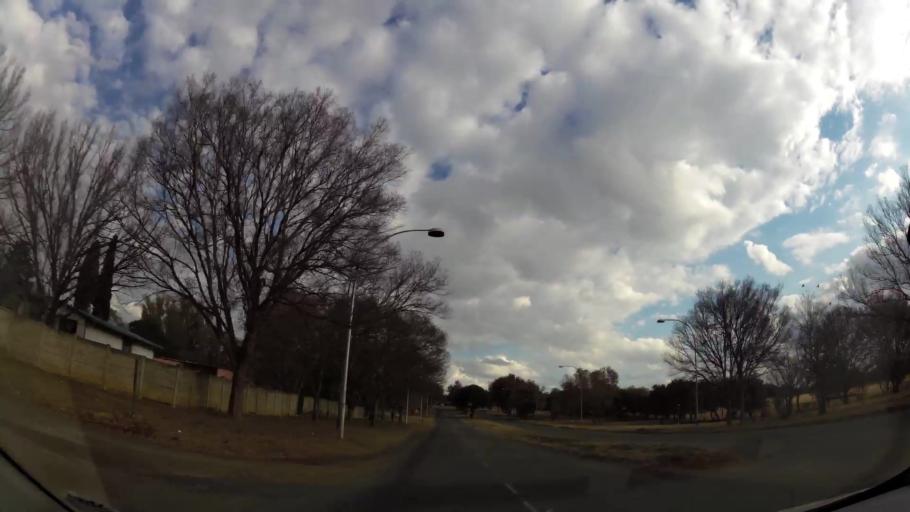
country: ZA
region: Orange Free State
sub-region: Fezile Dabi District Municipality
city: Sasolburg
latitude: -26.8087
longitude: 27.8107
